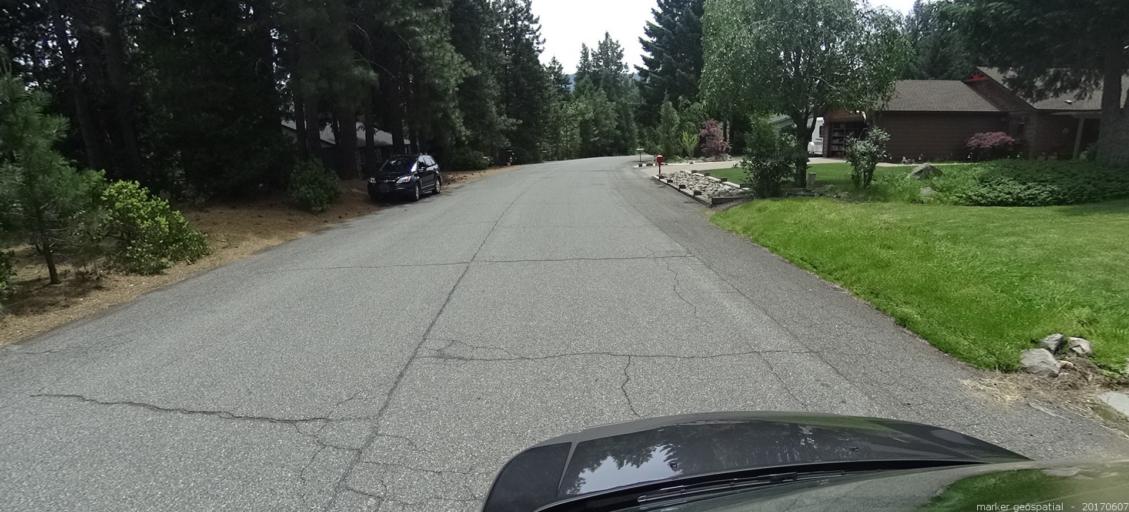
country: US
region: California
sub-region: Siskiyou County
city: Mount Shasta
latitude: 41.2898
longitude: -122.3229
